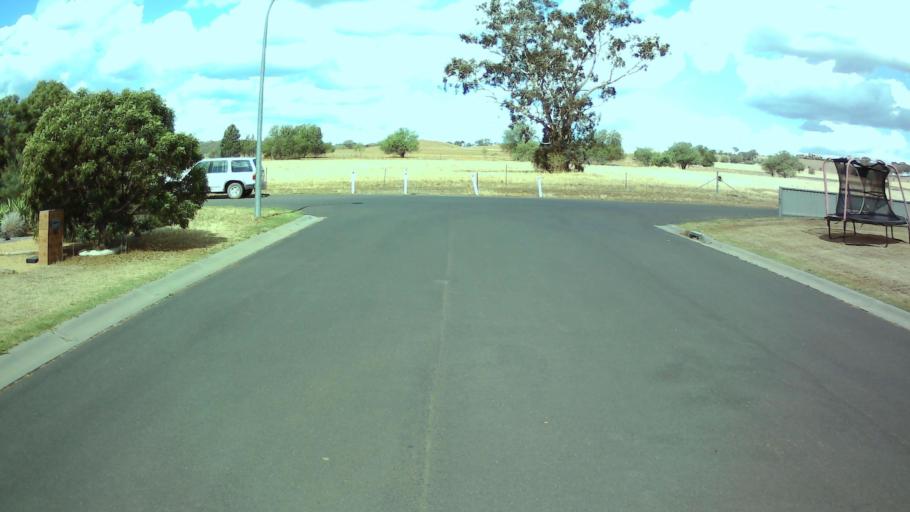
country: AU
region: New South Wales
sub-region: Weddin
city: Grenfell
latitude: -33.9078
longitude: 148.1637
